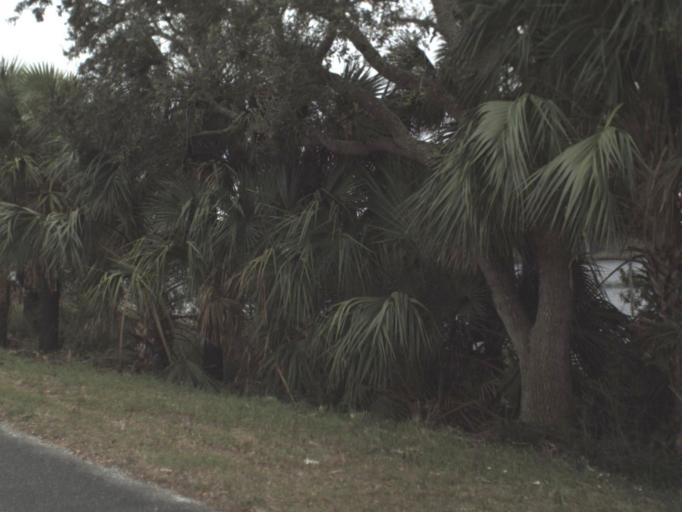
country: US
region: Florida
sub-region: Franklin County
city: Eastpoint
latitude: 29.8218
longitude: -84.8522
